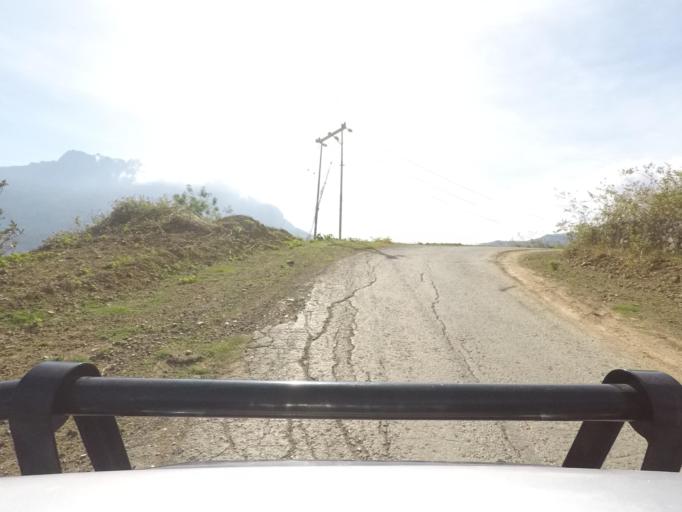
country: TL
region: Bobonaro
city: Maliana
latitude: -9.0080
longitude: 125.2492
